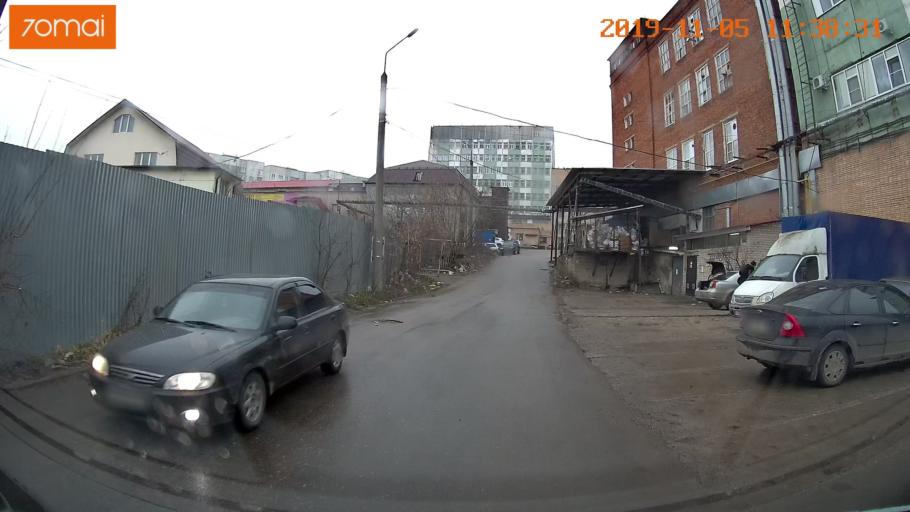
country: RU
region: Ivanovo
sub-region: Gorod Ivanovo
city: Ivanovo
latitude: 57.0105
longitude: 40.9583
